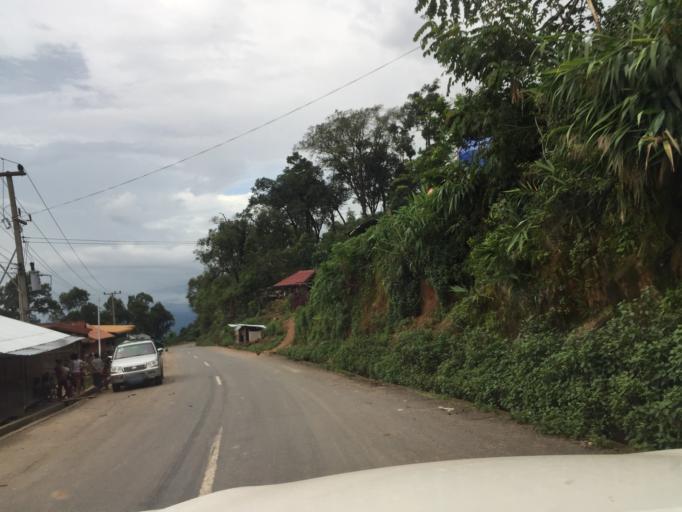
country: LA
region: Phongsali
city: Phongsali
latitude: 21.3204
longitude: 102.0487
